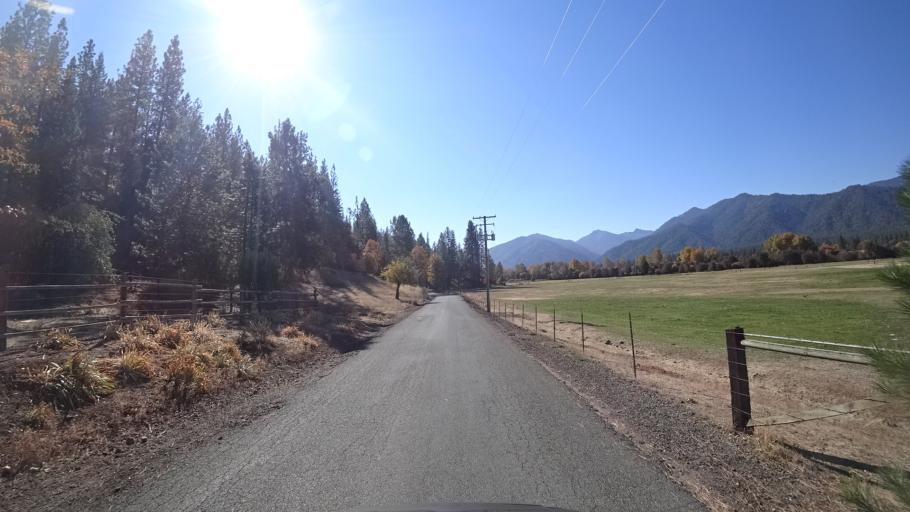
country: US
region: California
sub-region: Siskiyou County
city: Yreka
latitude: 41.5852
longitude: -122.9567
